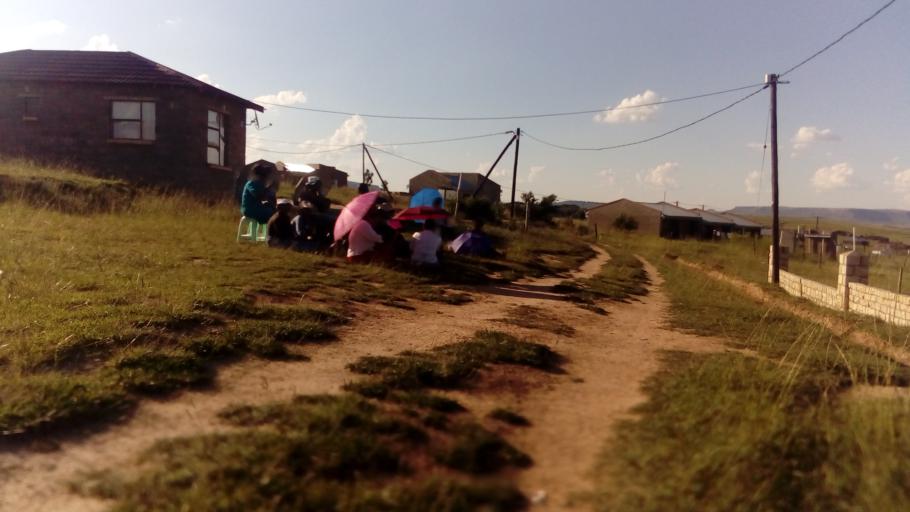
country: LS
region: Berea
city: Teyateyaneng
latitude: -29.1310
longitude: 27.7630
